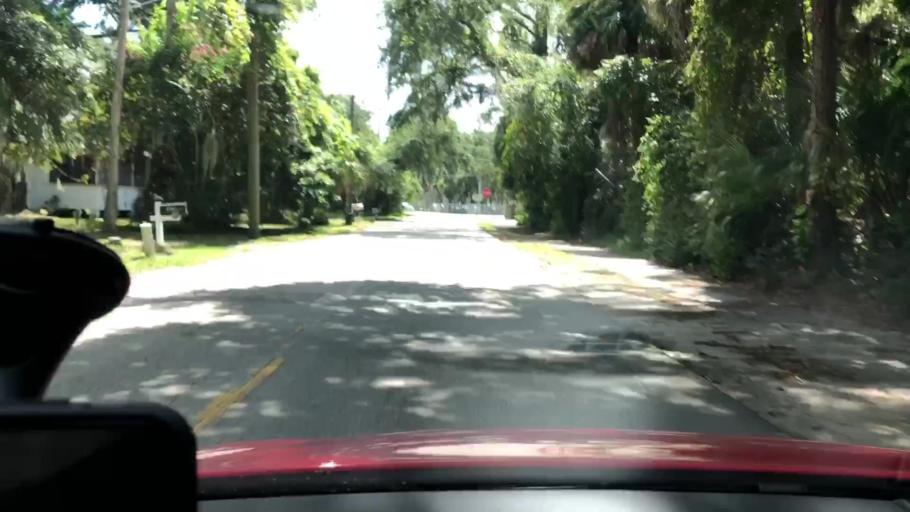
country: US
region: Florida
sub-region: Volusia County
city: New Smyrna Beach
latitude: 29.0072
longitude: -80.9239
